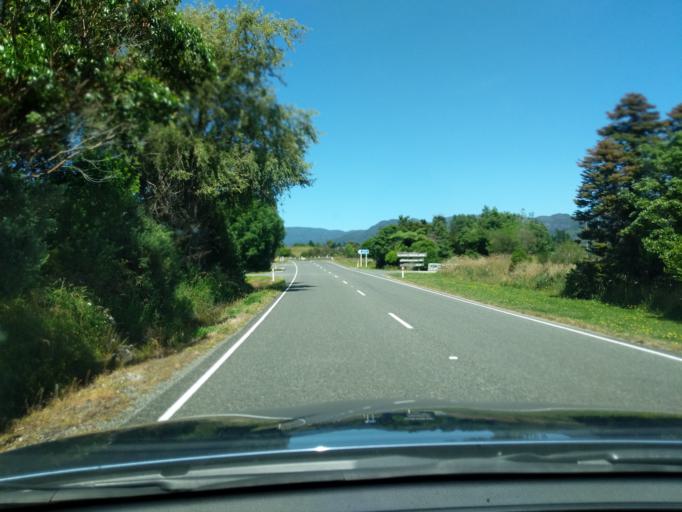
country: NZ
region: Tasman
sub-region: Tasman District
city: Takaka
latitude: -40.6825
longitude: 172.6636
